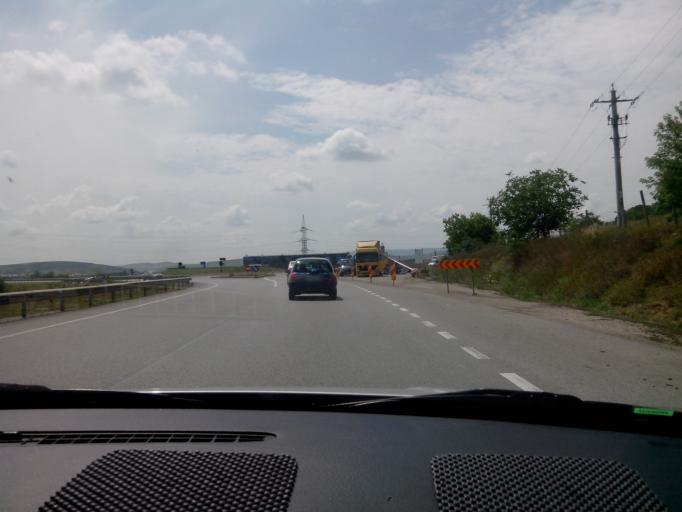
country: RO
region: Cluj
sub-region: Comuna Apahida
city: Apahida
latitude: 46.8234
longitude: 23.7445
